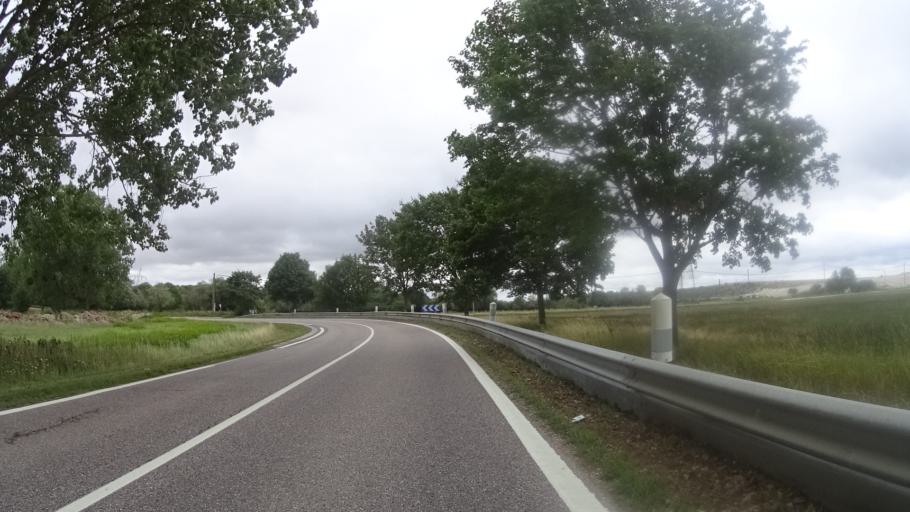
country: FR
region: Lorraine
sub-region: Departement de Meurthe-et-Moselle
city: Art-sur-Meurthe
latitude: 48.6583
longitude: 6.2541
